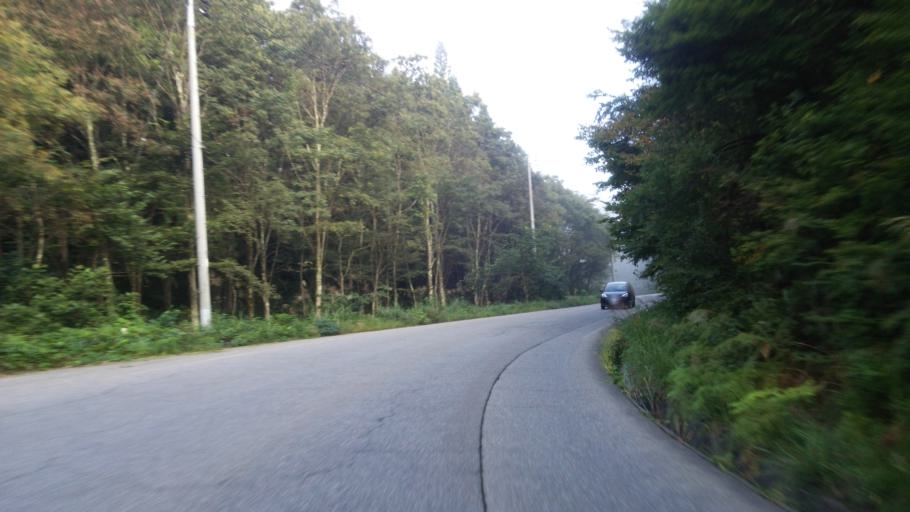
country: JP
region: Fukushima
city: Kitakata
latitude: 37.5738
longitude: 139.7808
